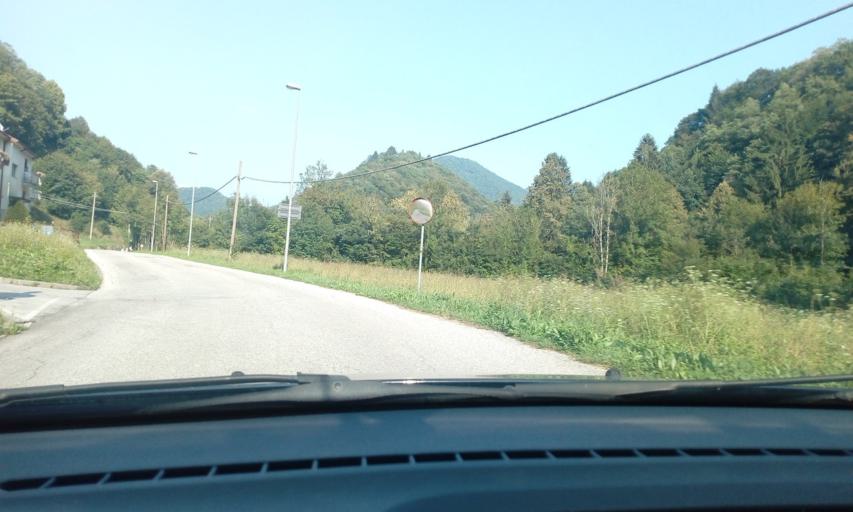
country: IT
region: Friuli Venezia Giulia
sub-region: Provincia di Udine
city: Clodig
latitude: 46.1552
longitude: 13.5881
